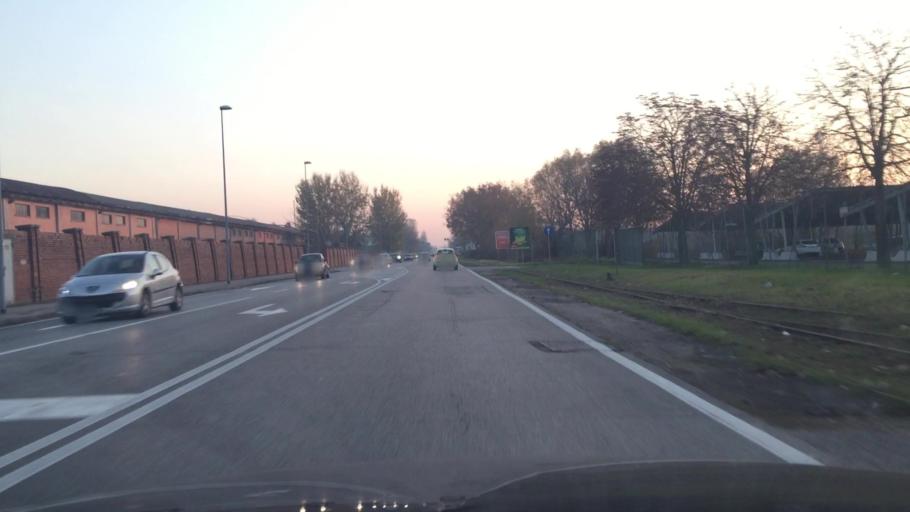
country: IT
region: Emilia-Romagna
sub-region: Provincia di Ferrara
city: Ferrara
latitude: 44.8578
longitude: 11.6011
